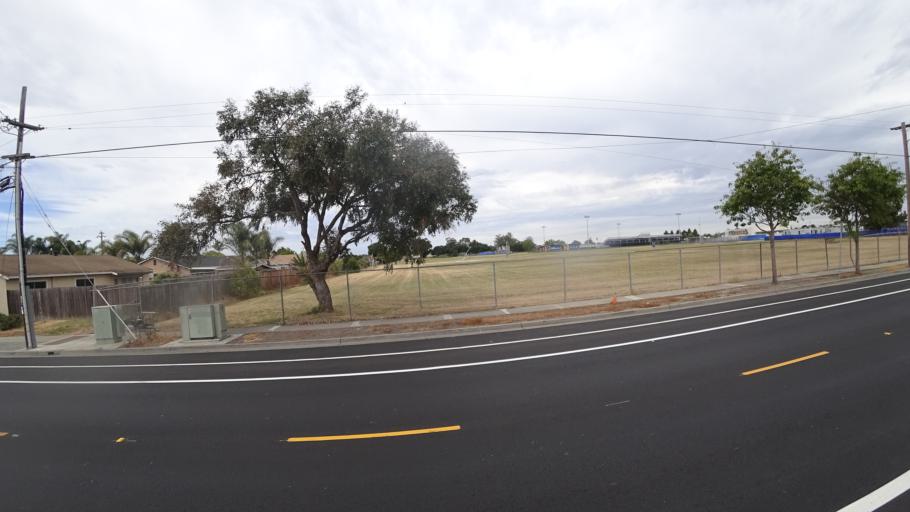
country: US
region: California
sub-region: Alameda County
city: Hayward
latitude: 37.6223
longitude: -122.0868
